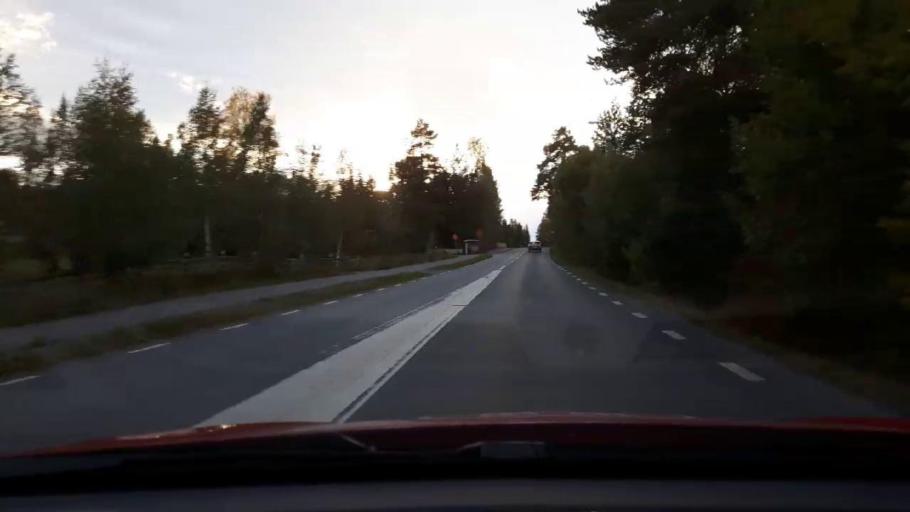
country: SE
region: Jaemtland
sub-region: OEstersunds Kommun
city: Ostersund
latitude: 63.1520
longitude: 14.5884
